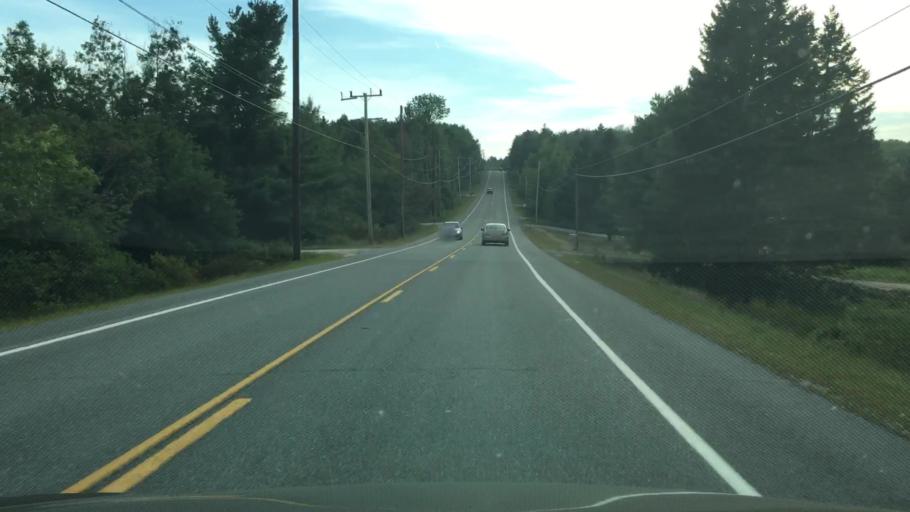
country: US
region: Maine
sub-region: Hancock County
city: Surry
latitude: 44.4581
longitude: -68.5445
